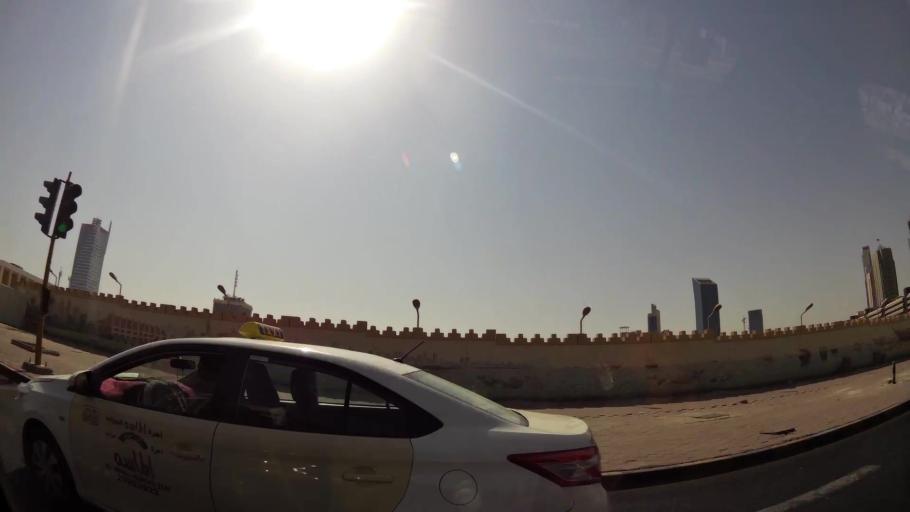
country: KW
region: Al Asimah
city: Kuwait City
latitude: 29.3660
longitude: 47.9709
